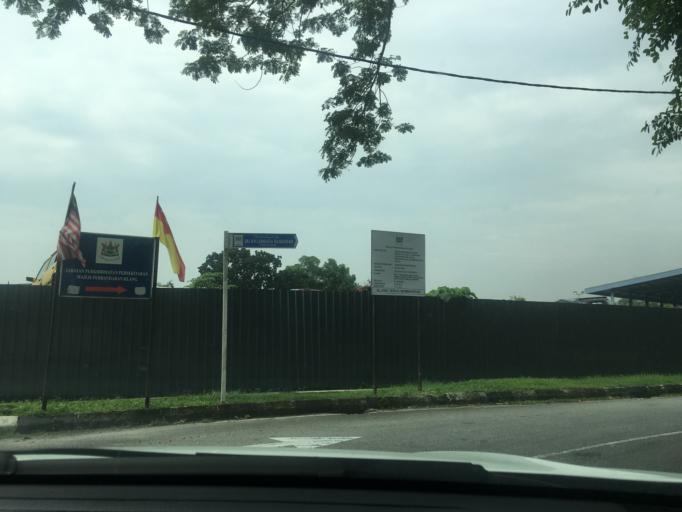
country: MY
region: Selangor
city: Klang
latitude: 3.0470
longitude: 101.4404
